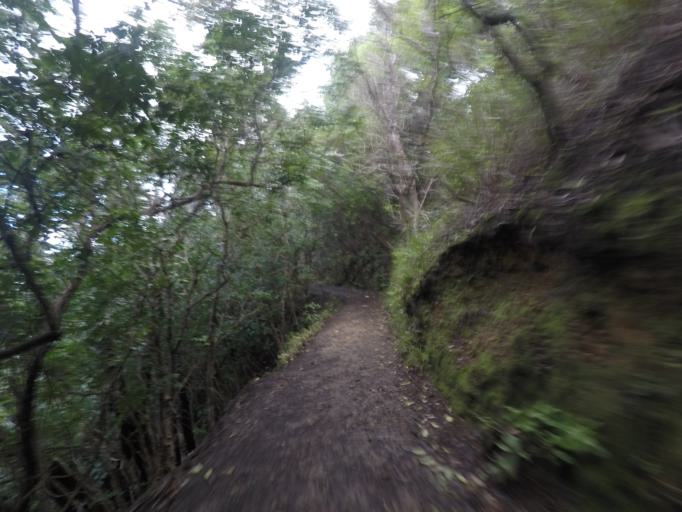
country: NZ
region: Bay of Plenty
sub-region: Western Bay of Plenty District
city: Waihi Beach
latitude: -37.3921
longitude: 175.9406
